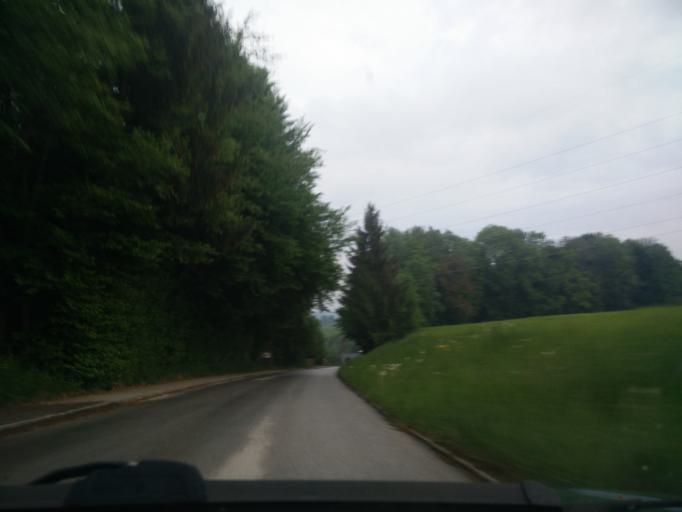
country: AT
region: Salzburg
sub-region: Politischer Bezirk Salzburg-Umgebung
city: Eugendorf
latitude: 47.8742
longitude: 13.1214
